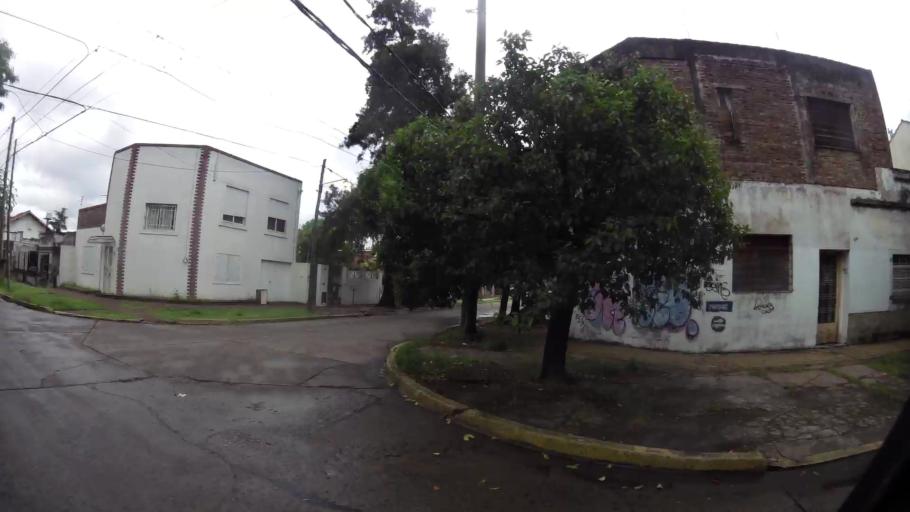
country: AR
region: Buenos Aires
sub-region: Partido de Lomas de Zamora
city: Lomas de Zamora
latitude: -34.7588
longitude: -58.3865
